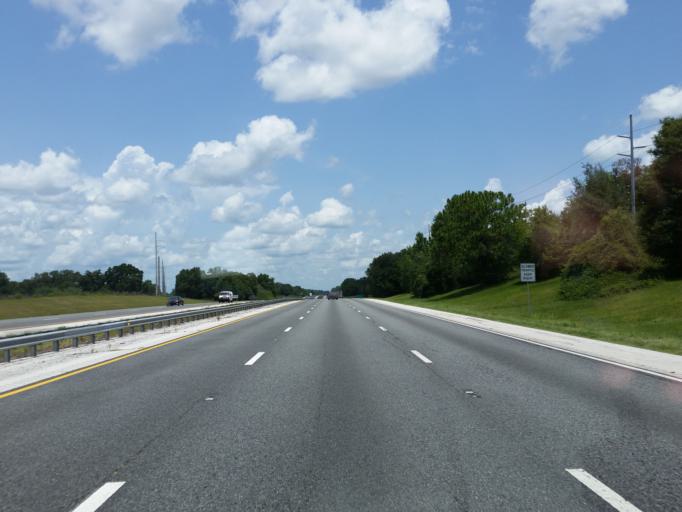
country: US
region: Florida
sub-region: Marion County
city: Ocala
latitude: 29.2773
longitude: -82.1967
